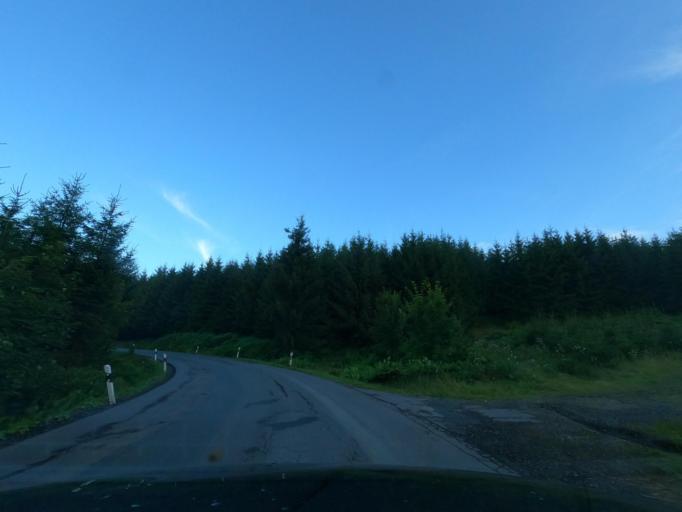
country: DE
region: North Rhine-Westphalia
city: Plettenberg
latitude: 51.2539
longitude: 7.9209
